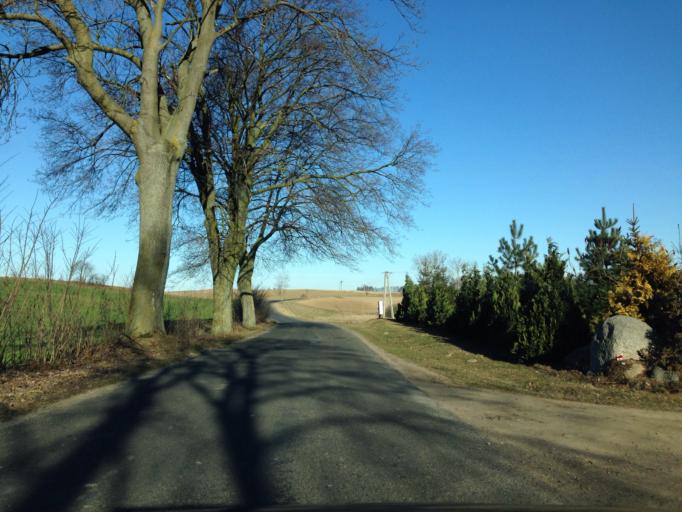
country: PL
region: Warmian-Masurian Voivodeship
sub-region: Powiat nowomiejski
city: Nowe Miasto Lubawskie
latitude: 53.3883
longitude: 19.6156
